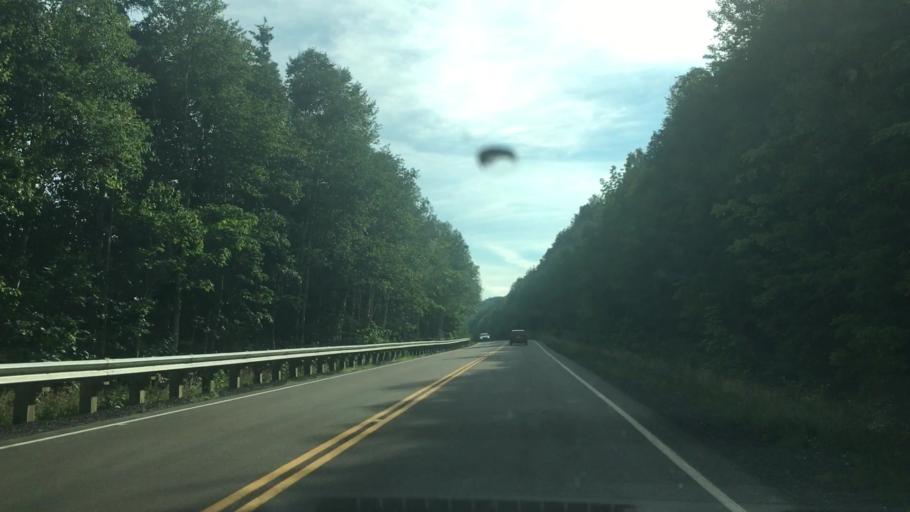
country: CA
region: Nova Scotia
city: Sydney Mines
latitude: 46.8263
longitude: -60.6225
